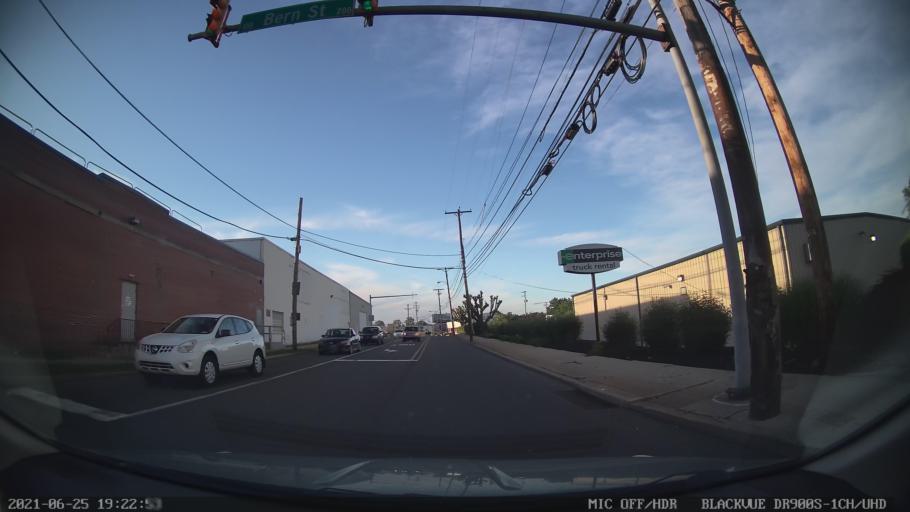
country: US
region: Pennsylvania
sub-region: Berks County
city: Hyde Park
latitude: 40.3625
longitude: -75.9326
